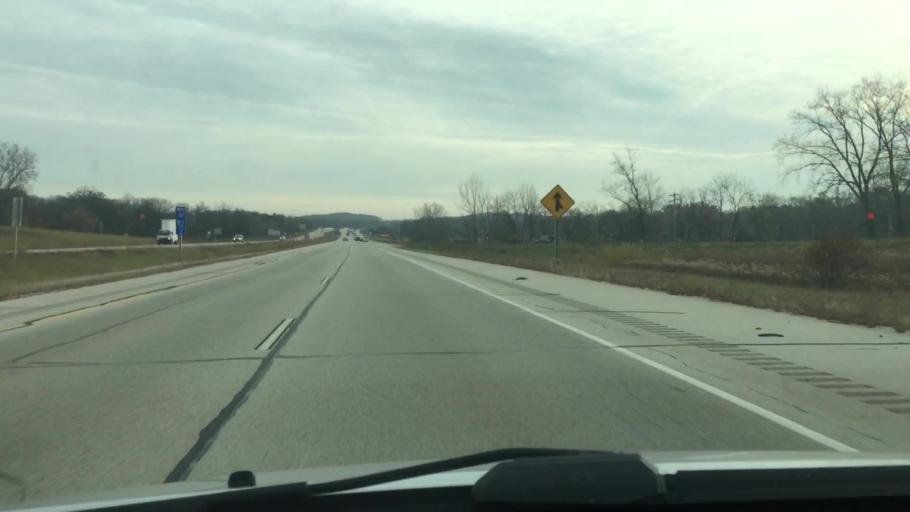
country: US
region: Wisconsin
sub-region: Waukesha County
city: Muskego
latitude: 42.9336
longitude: -88.1575
